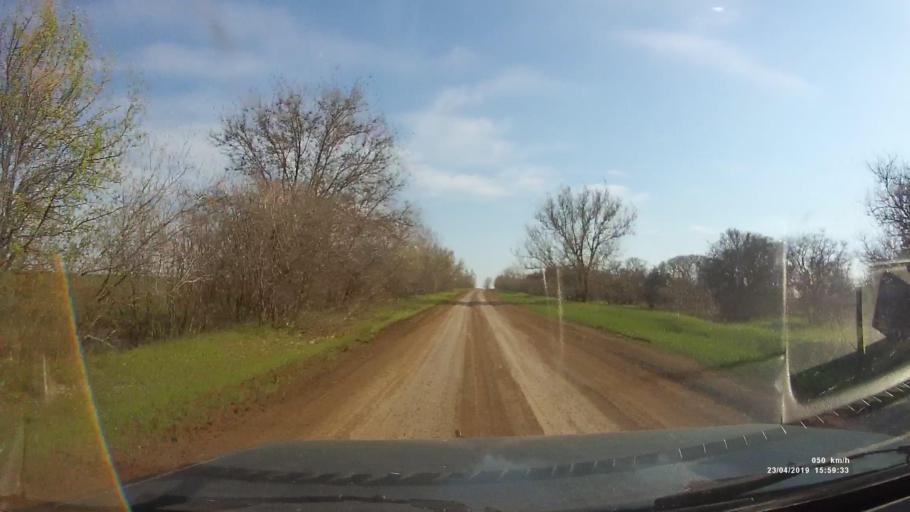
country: RU
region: Rostov
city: Remontnoye
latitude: 46.5160
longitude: 43.1096
